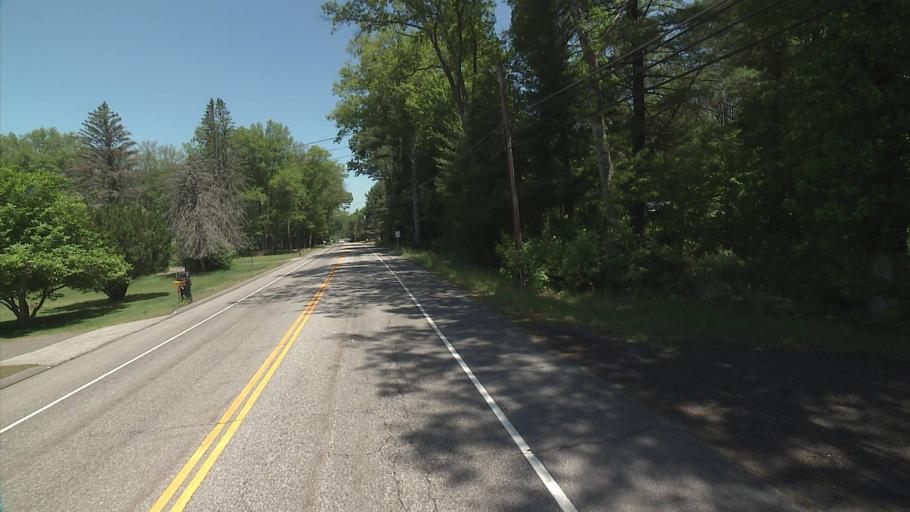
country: US
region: Connecticut
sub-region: Tolland County
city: Crystal Lake
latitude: 41.9156
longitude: -72.3902
